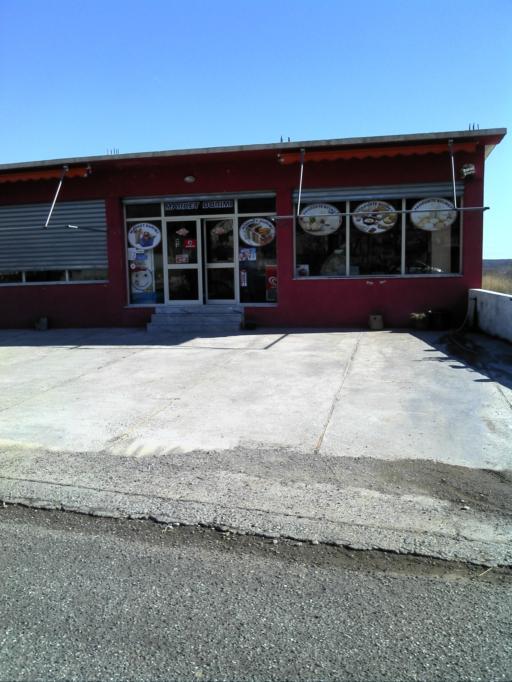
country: AL
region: Shkoder
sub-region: Rrethi i Shkodres
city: Berdica e Madhe
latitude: 42.0262
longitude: 19.4692
